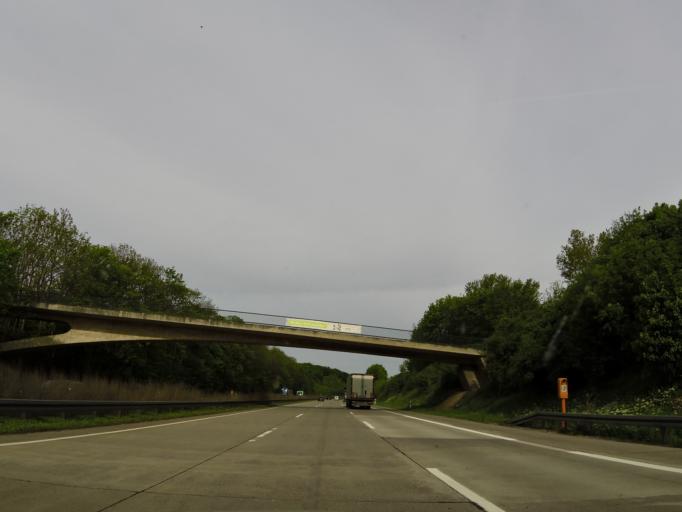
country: DE
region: Lower Saxony
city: Hildesheim
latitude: 52.1352
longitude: 10.0211
